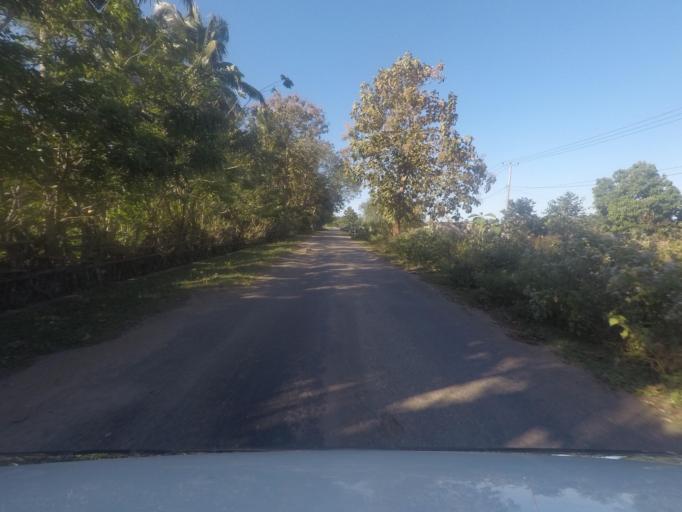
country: TL
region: Lautem
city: Lospalos
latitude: -8.4039
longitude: 127.1772
